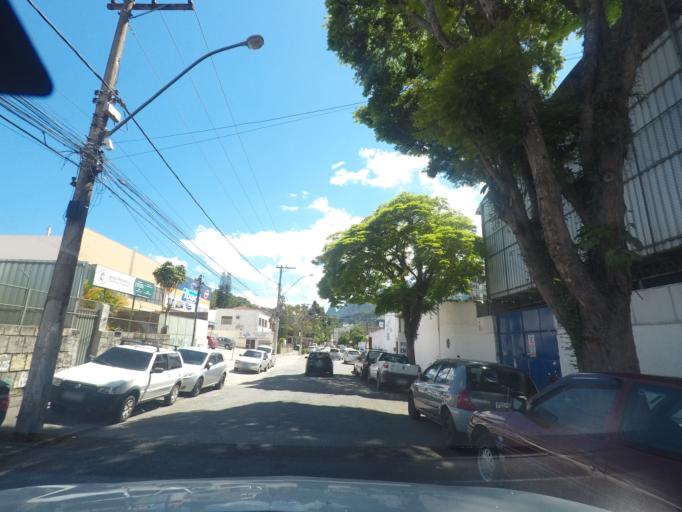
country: BR
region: Rio de Janeiro
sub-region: Teresopolis
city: Teresopolis
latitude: -22.4191
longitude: -42.9727
